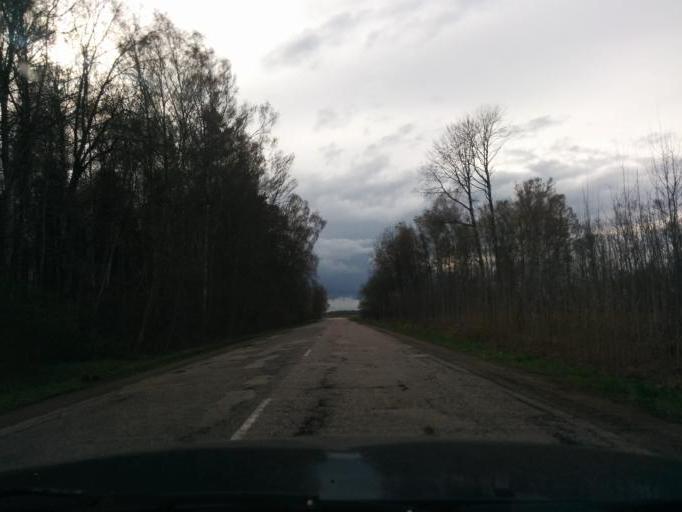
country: LT
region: Siauliu apskritis
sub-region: Joniskis
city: Joniskis
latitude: 56.4173
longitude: 23.5962
